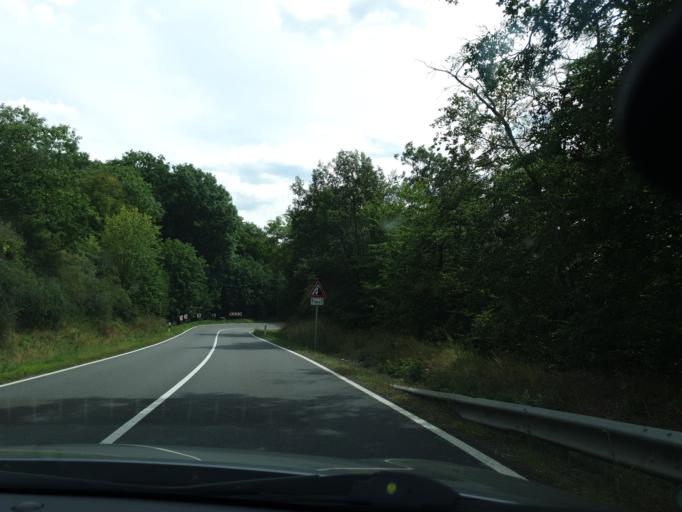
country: DE
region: Rheinland-Pfalz
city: Weiler
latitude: 50.3276
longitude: 7.1250
